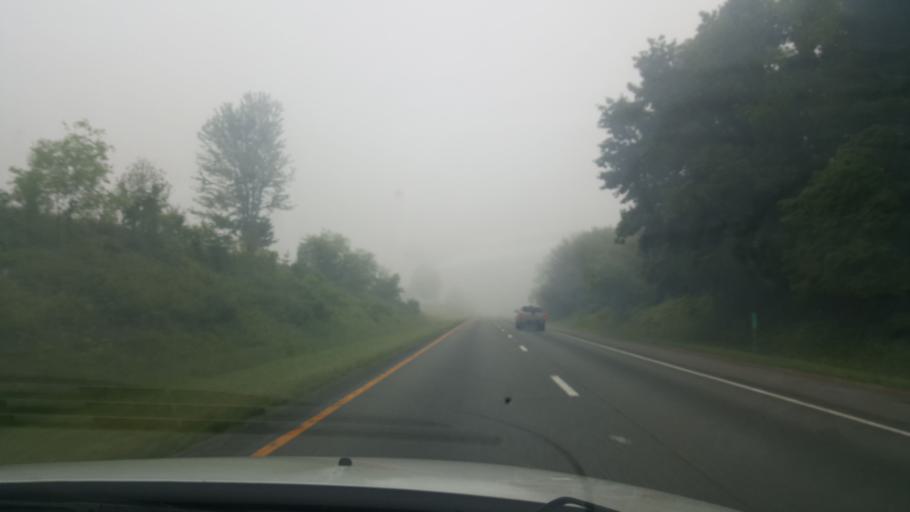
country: US
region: Virginia
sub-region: Montgomery County
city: Christiansburg
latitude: 37.1181
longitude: -80.4129
